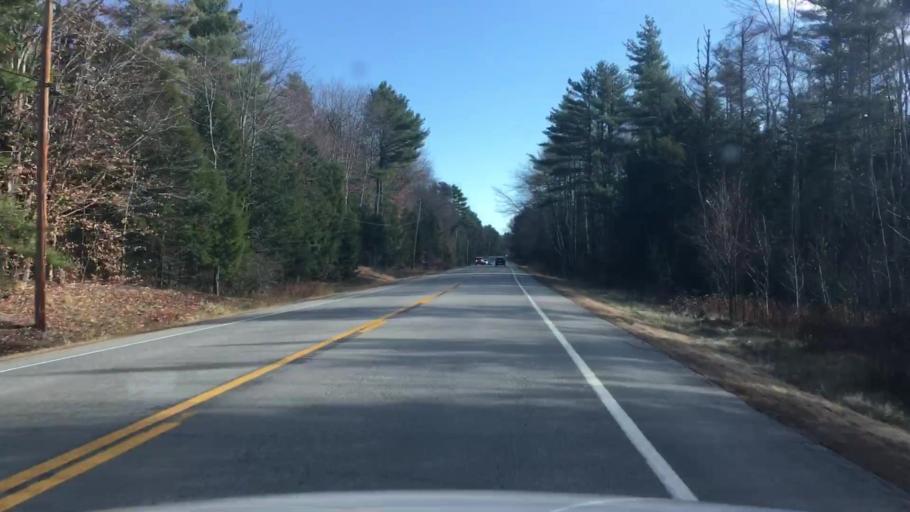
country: US
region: Maine
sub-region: Lincoln County
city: Jefferson
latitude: 44.2603
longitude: -69.4551
